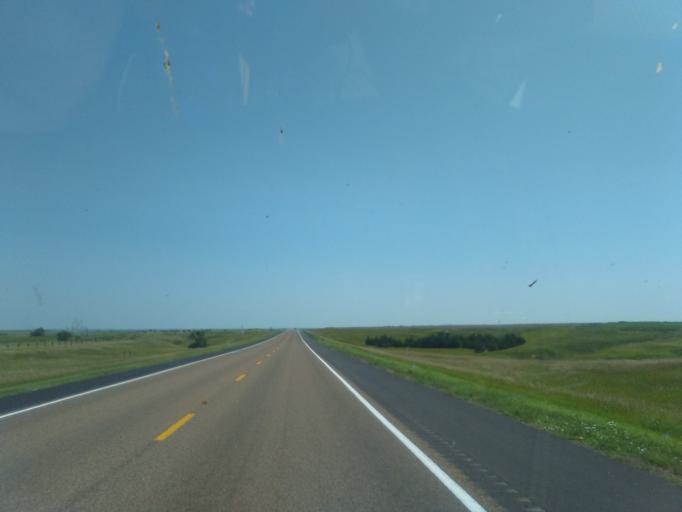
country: US
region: Nebraska
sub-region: Hitchcock County
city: Trenton
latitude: 40.2266
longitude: -100.9249
